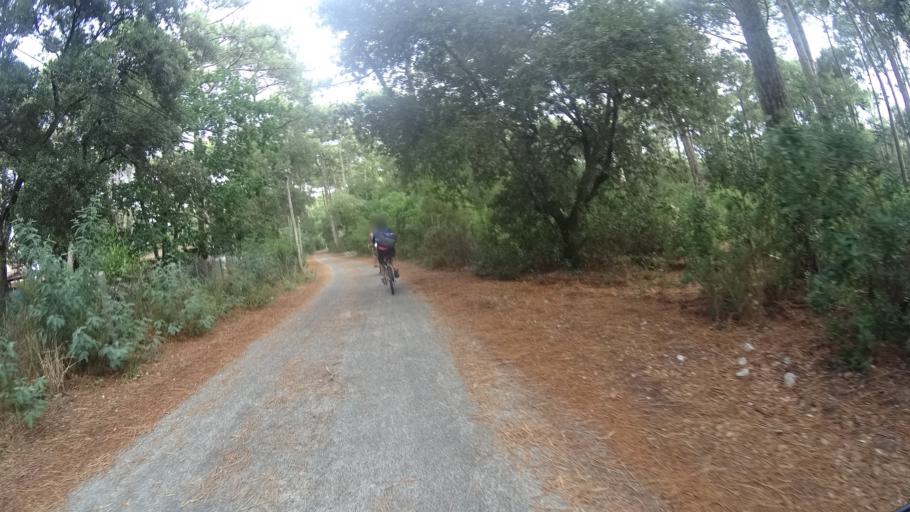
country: FR
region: Aquitaine
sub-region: Departement de la Gironde
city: Lacanau
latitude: 44.9903
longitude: -1.1421
